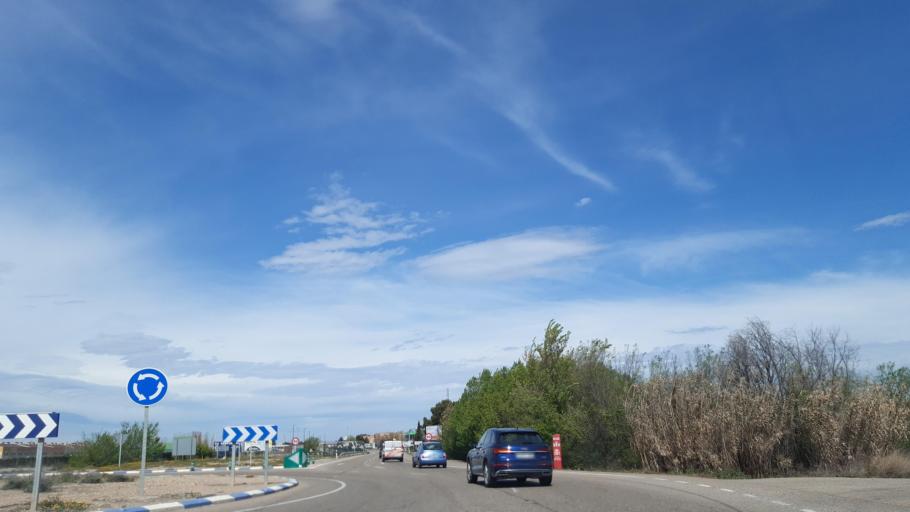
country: ES
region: Aragon
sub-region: Provincia de Zaragoza
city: Utebo
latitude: 41.6983
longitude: -0.9938
